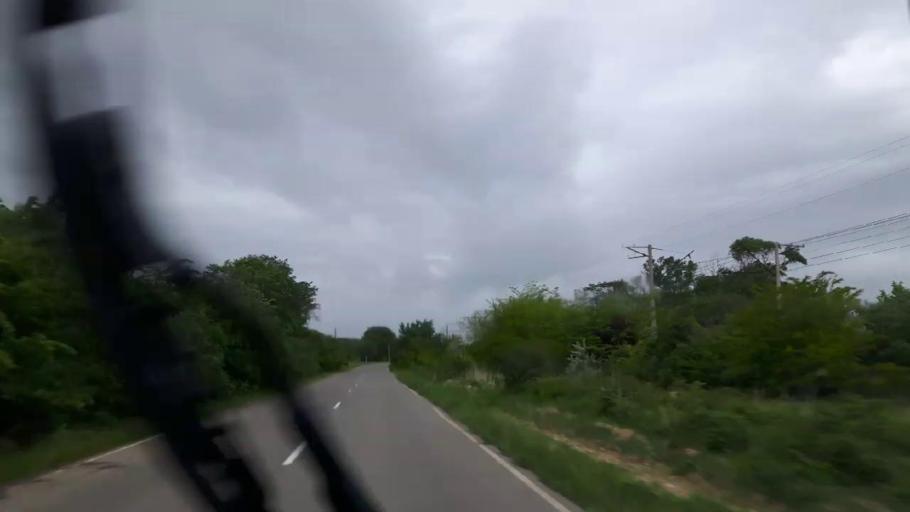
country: GE
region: Shida Kartli
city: Gori
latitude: 41.9938
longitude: 44.0290
